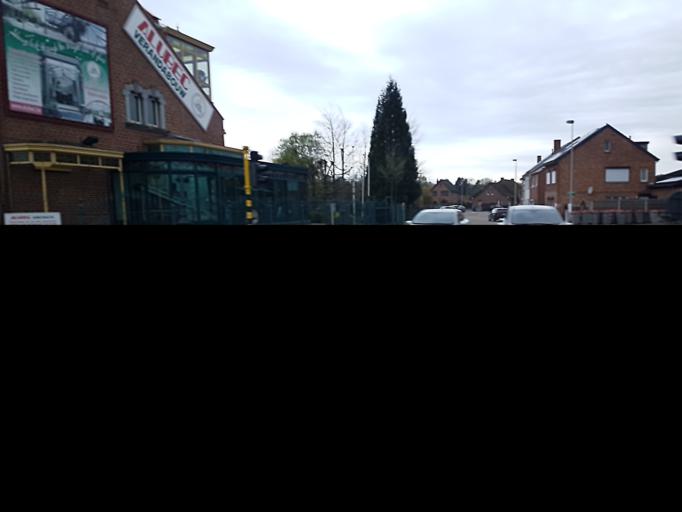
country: BE
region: Flanders
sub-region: Provincie Limburg
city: Lanaken
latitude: 50.9184
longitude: 5.6842
